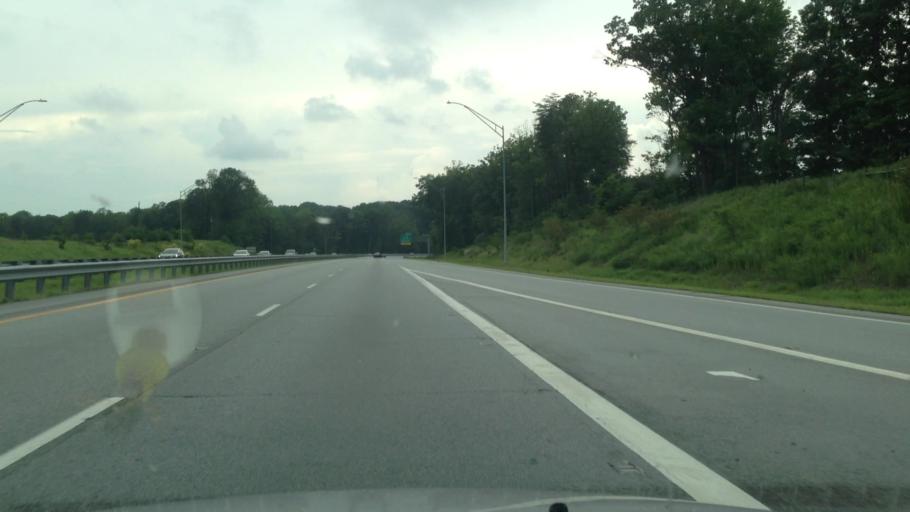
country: US
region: North Carolina
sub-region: Forsyth County
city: Kernersville
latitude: 36.1075
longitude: -80.0504
